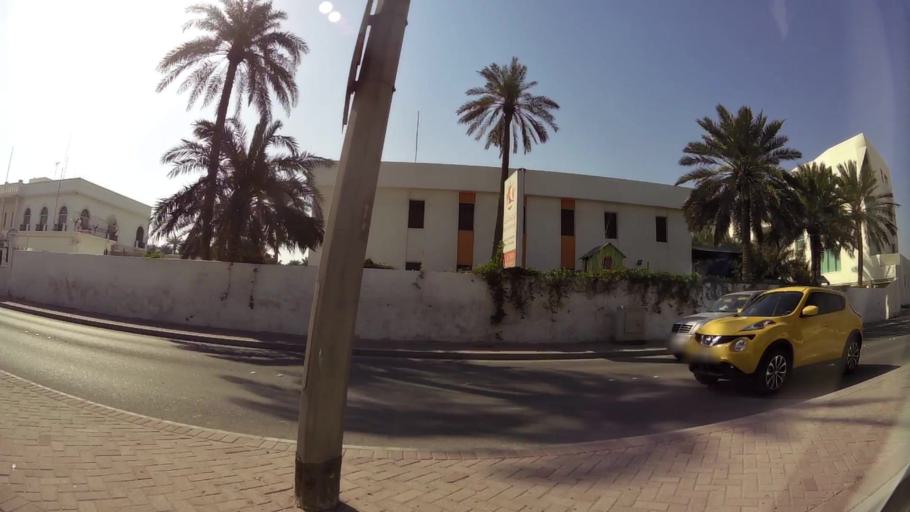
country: BH
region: Manama
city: Manama
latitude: 26.2199
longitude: 50.5804
